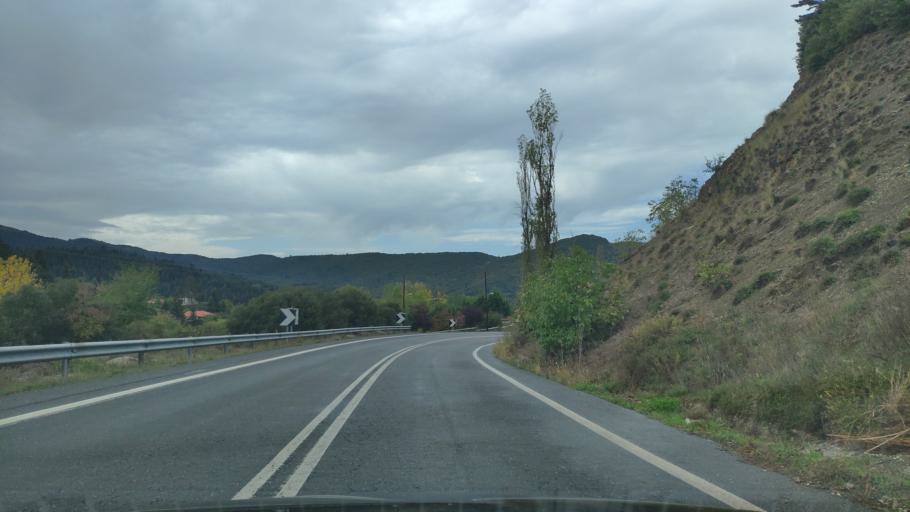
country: GR
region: Peloponnese
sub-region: Nomos Arkadias
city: Dimitsana
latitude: 37.6361
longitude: 22.0894
